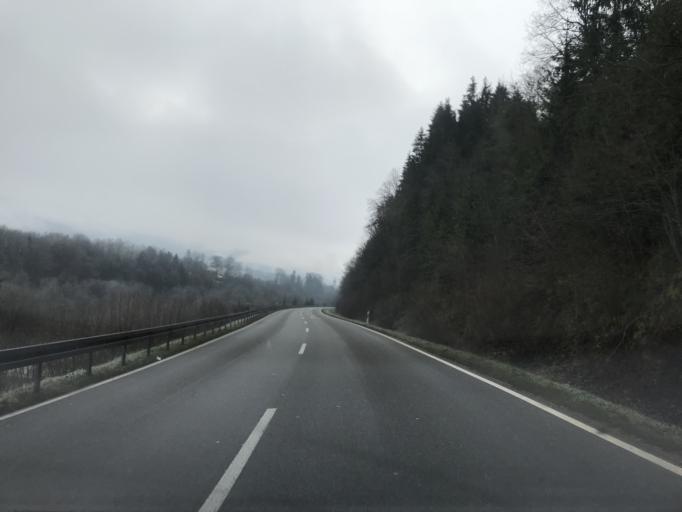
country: DE
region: Baden-Wuerttemberg
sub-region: Freiburg Region
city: Hasel
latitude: 47.6413
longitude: 7.8936
